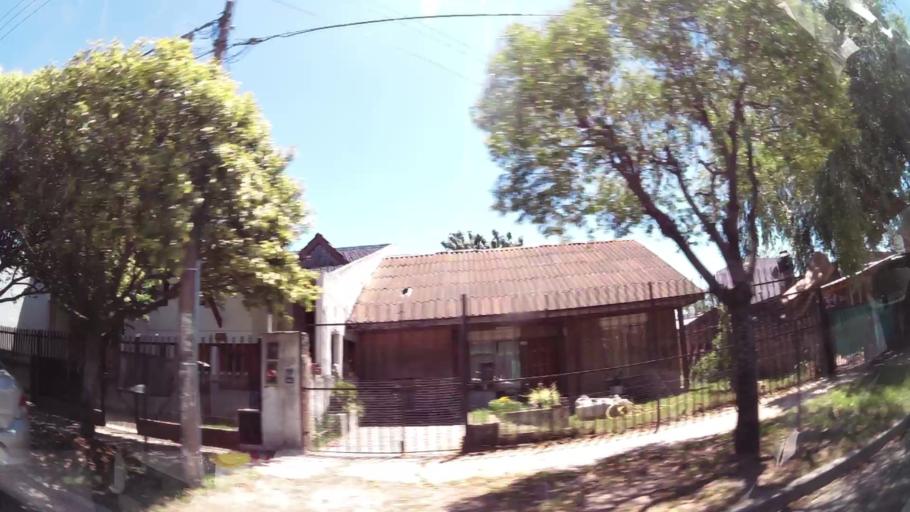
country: AR
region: Buenos Aires
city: Hurlingham
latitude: -34.5114
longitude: -58.7076
